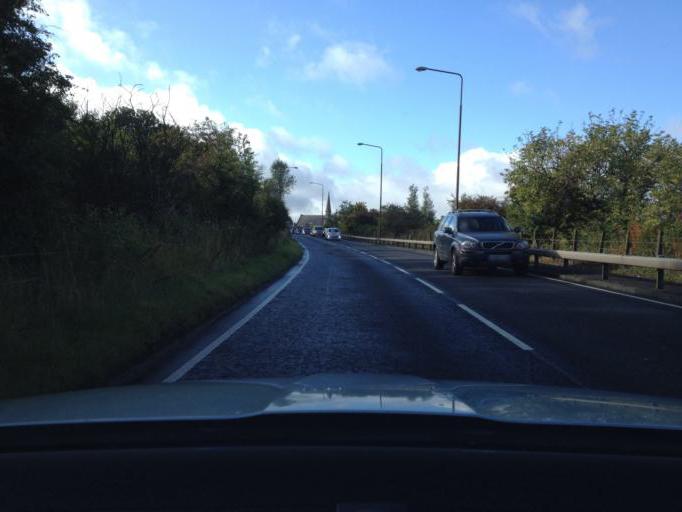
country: GB
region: Scotland
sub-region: West Lothian
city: West Calder
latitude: 55.8551
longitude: -3.5652
